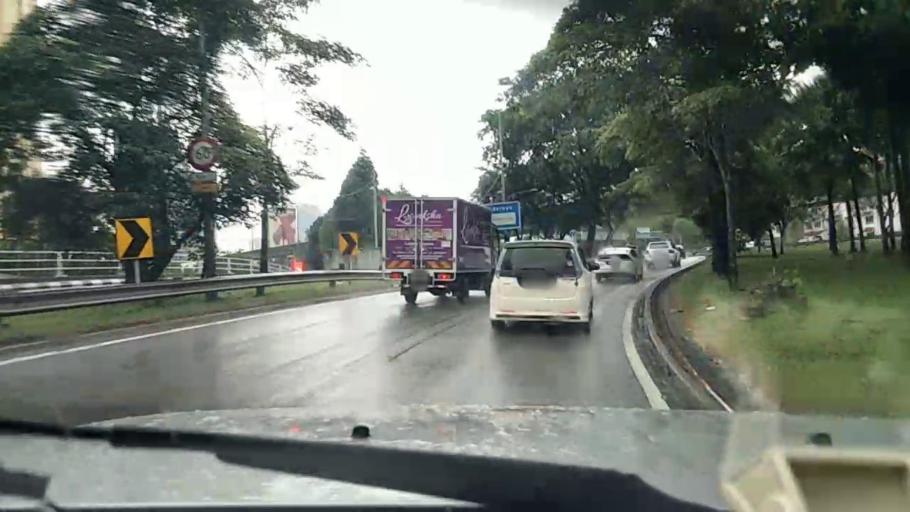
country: MY
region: Kuala Lumpur
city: Kuala Lumpur
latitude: 3.1166
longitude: 101.6786
